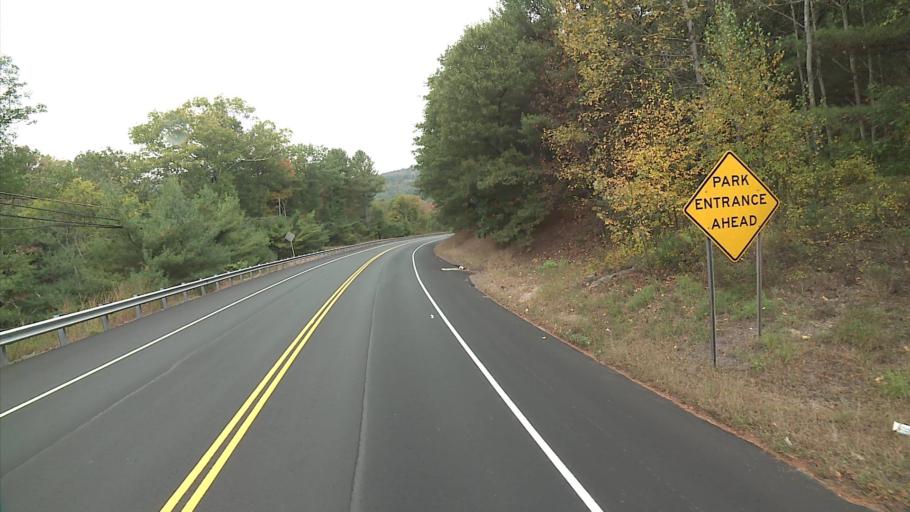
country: US
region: Connecticut
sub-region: Litchfield County
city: Thomaston
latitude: 41.6504
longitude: -73.0959
